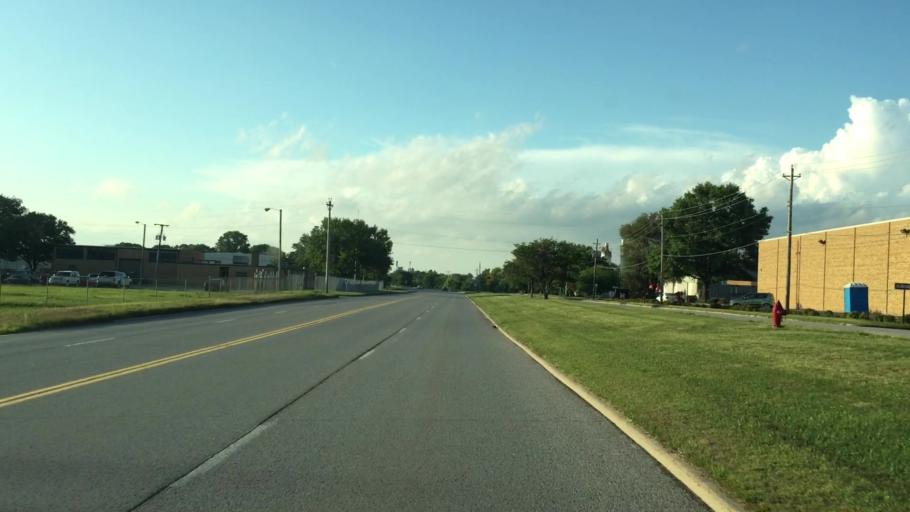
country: US
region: Iowa
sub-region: Johnson County
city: University Heights
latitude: 41.6356
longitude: -91.5385
